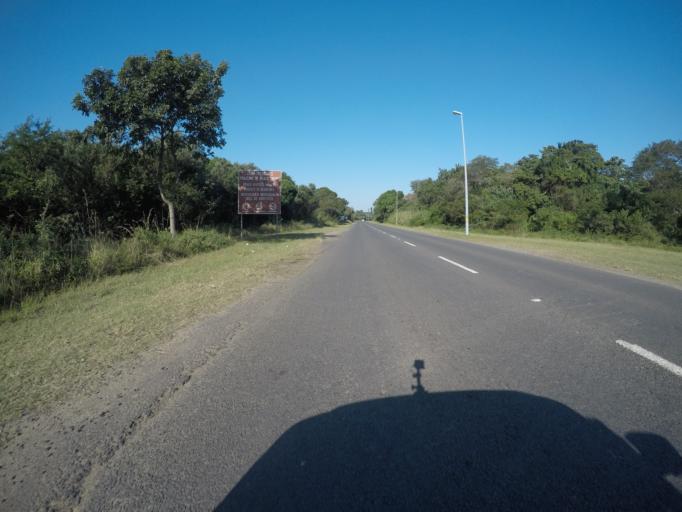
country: ZA
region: KwaZulu-Natal
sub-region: uThungulu District Municipality
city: Richards Bay
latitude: -28.7865
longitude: 32.0849
